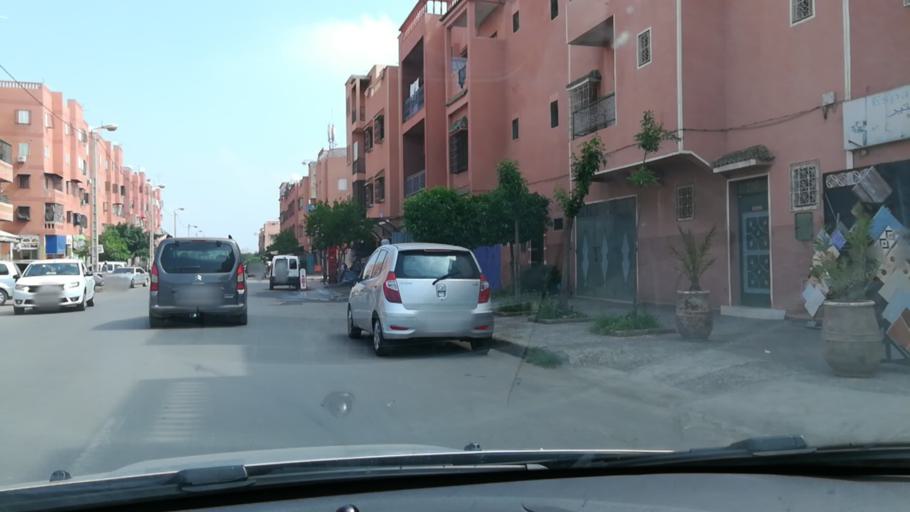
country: MA
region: Marrakech-Tensift-Al Haouz
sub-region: Marrakech
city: Marrakesh
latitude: 31.6351
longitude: -8.0623
